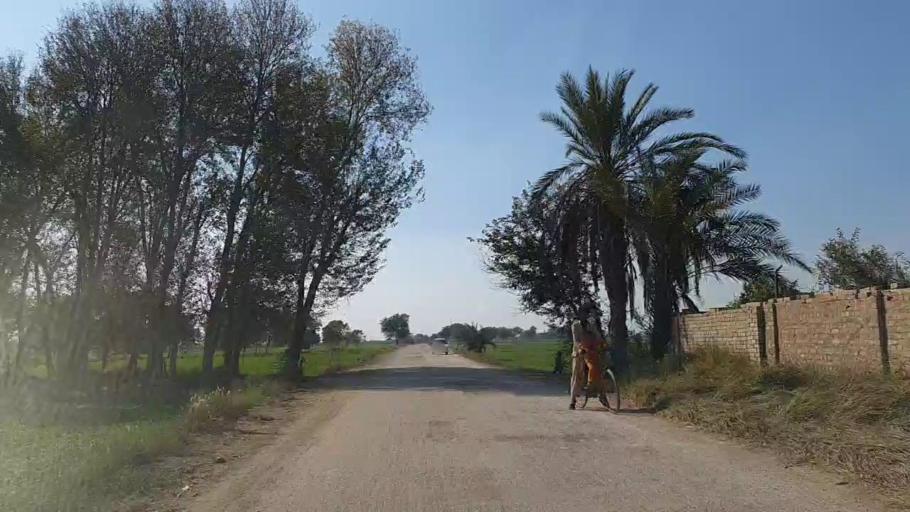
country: PK
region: Sindh
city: Daur
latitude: 26.3511
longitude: 68.3588
